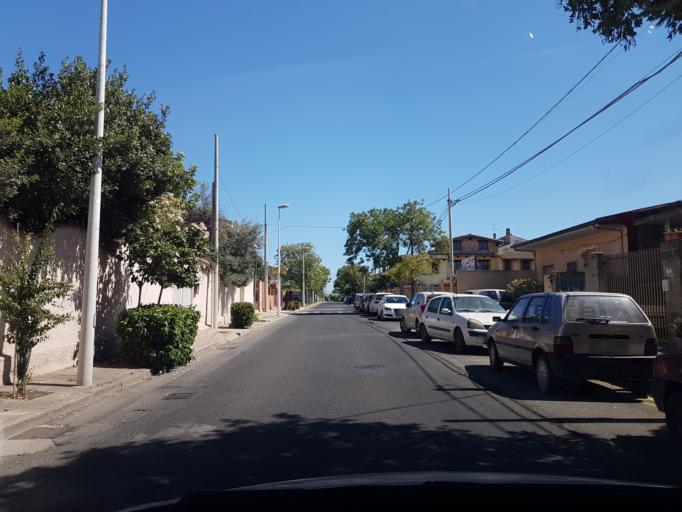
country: IT
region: Sardinia
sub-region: Provincia di Oristano
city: Cabras
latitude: 39.9235
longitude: 8.5339
